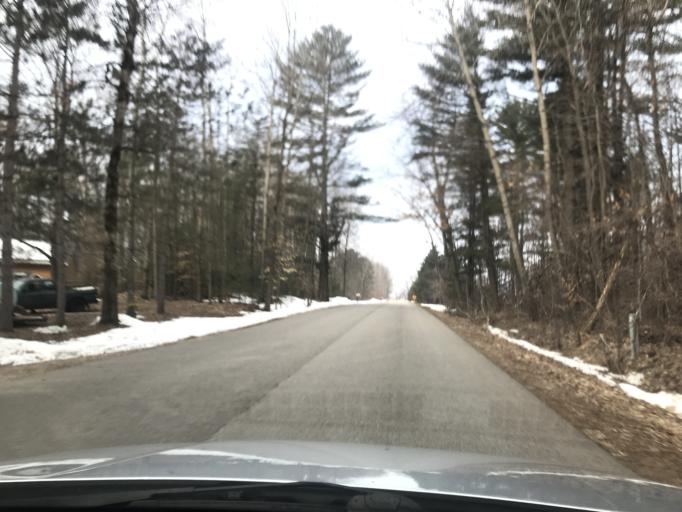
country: US
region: Wisconsin
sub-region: Oconto County
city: Oconto Falls
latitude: 44.8297
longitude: -88.1822
